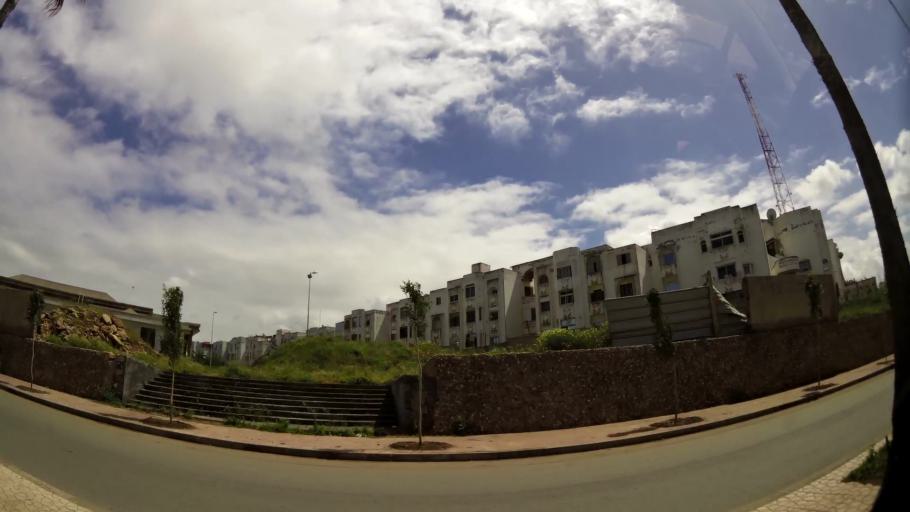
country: MA
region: Grand Casablanca
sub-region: Mediouna
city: Tit Mellil
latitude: 33.6040
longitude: -7.5240
